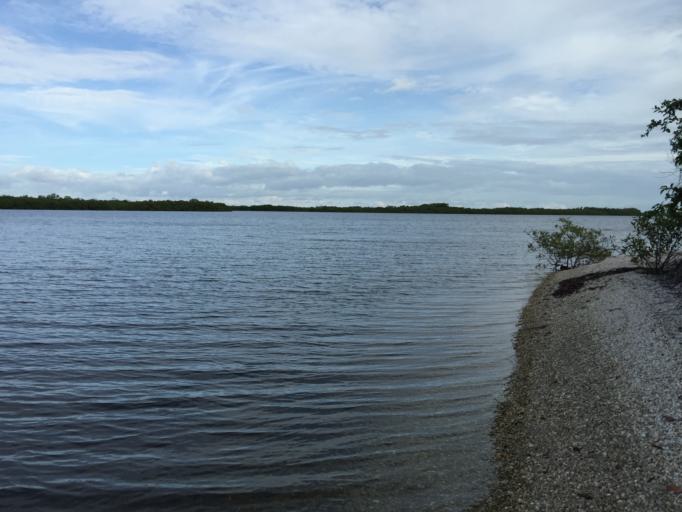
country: SN
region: Fatick
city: Sokone
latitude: 13.8343
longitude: -16.4971
